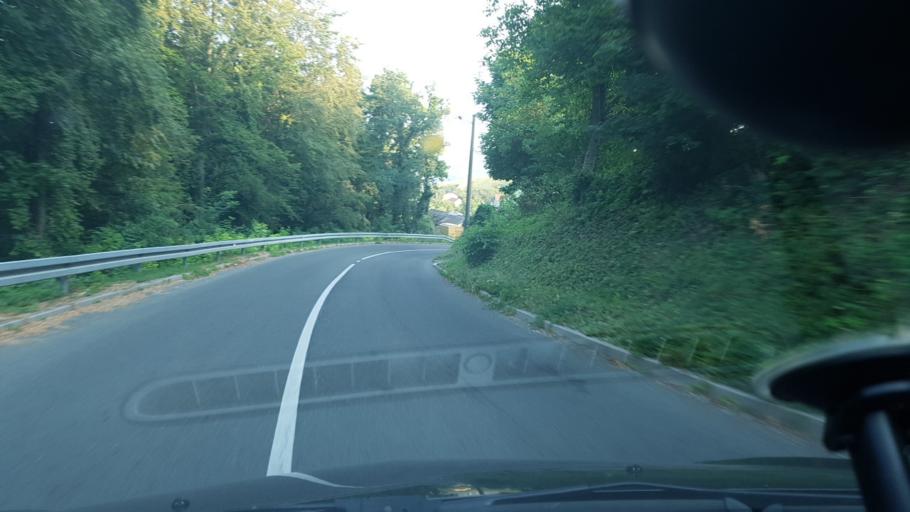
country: HR
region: Krapinsko-Zagorska
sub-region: Grad Krapina
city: Krapina
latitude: 46.1633
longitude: 15.8580
